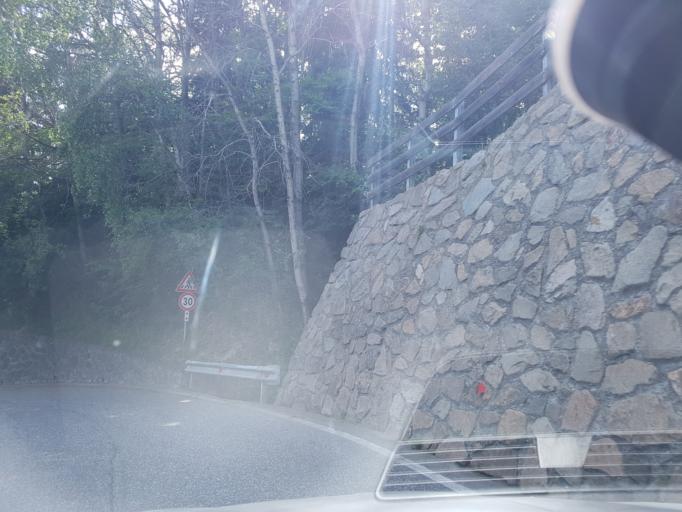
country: IT
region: Trentino-Alto Adige
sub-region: Bolzano
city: Villandro - Villanders
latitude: 46.6319
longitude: 11.5372
